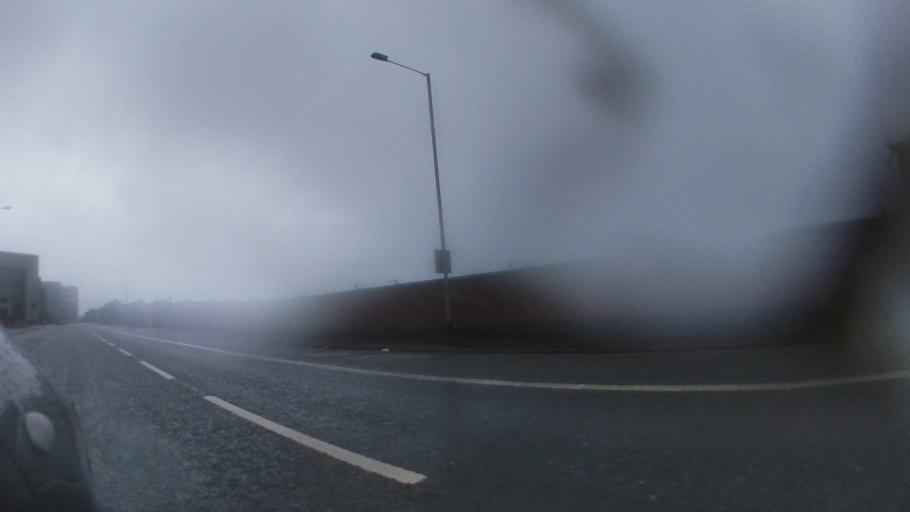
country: GB
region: Northern Ireland
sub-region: Castlereagh District
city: Castlereagh
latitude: 54.6124
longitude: -5.9018
